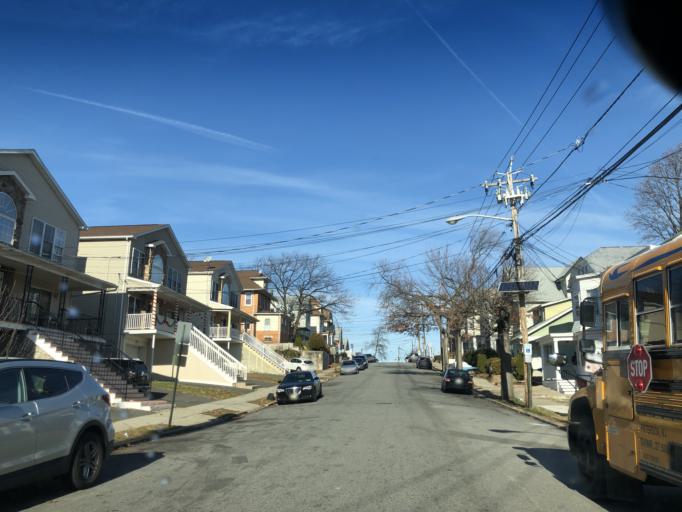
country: US
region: New Jersey
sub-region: Bergen County
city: Fair Lawn
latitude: 40.9198
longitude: -74.1454
